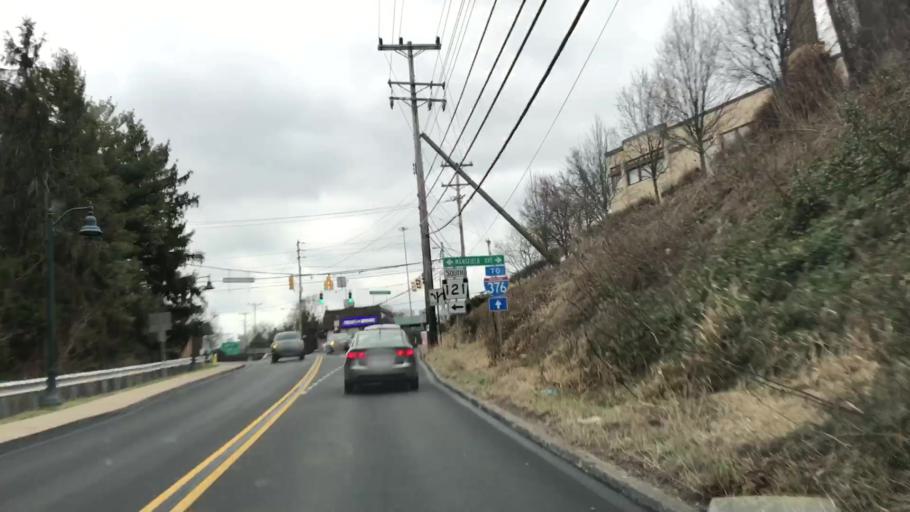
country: US
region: Pennsylvania
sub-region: Allegheny County
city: Green Tree
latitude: 40.4224
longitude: -80.0499
